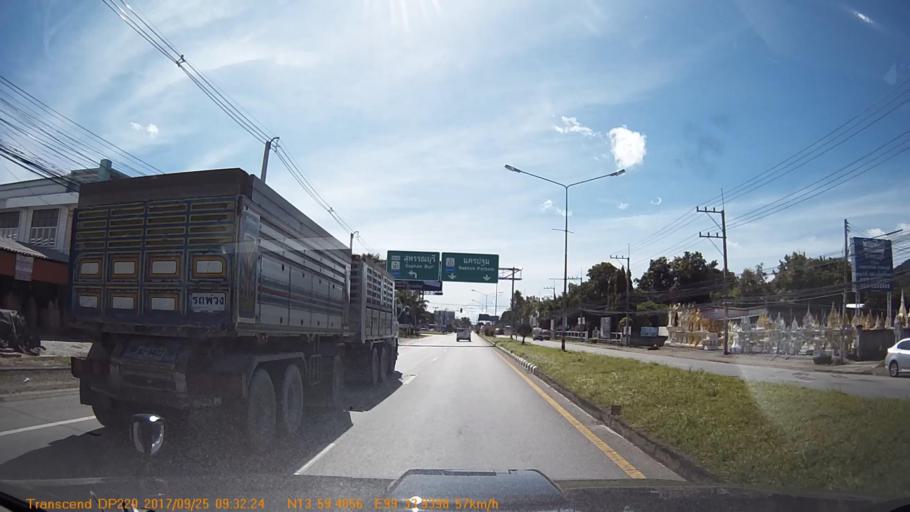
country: TH
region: Kanchanaburi
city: Kanchanaburi
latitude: 13.9914
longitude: 99.5657
